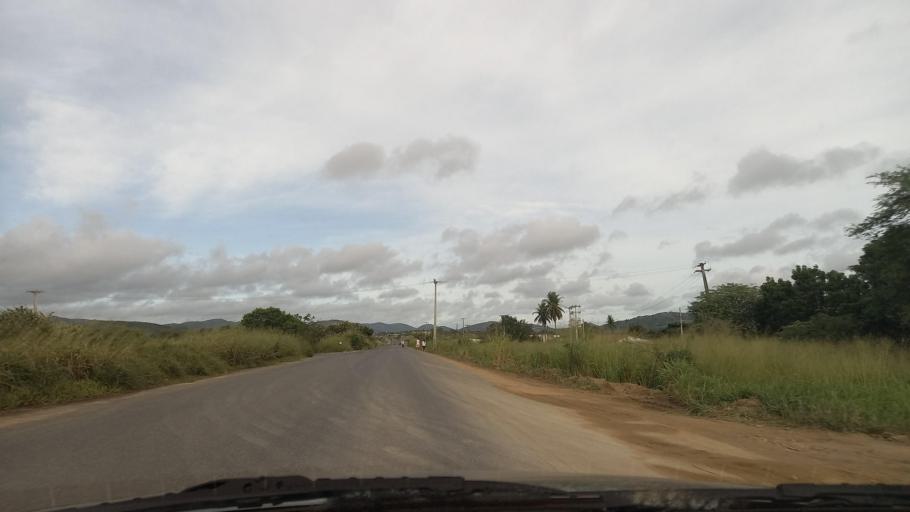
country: BR
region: Pernambuco
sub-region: Pombos
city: Pombos
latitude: -8.1265
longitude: -35.3497
